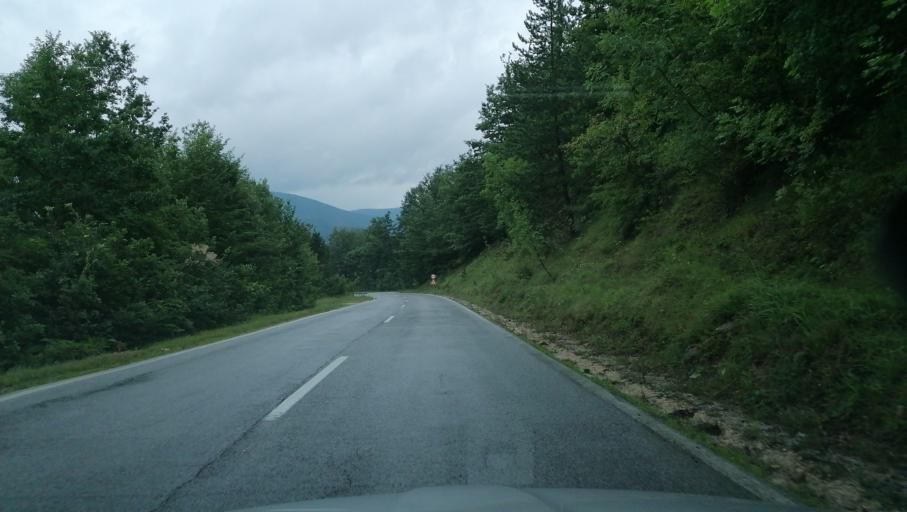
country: RS
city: Durici
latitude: 43.8068
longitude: 19.5105
